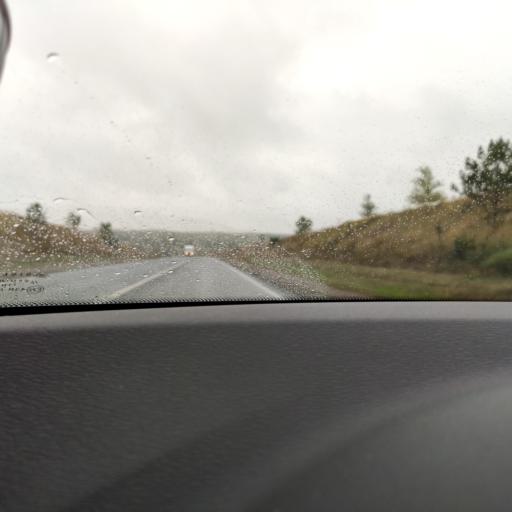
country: RU
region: Samara
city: Bereza
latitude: 53.6522
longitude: 50.2168
